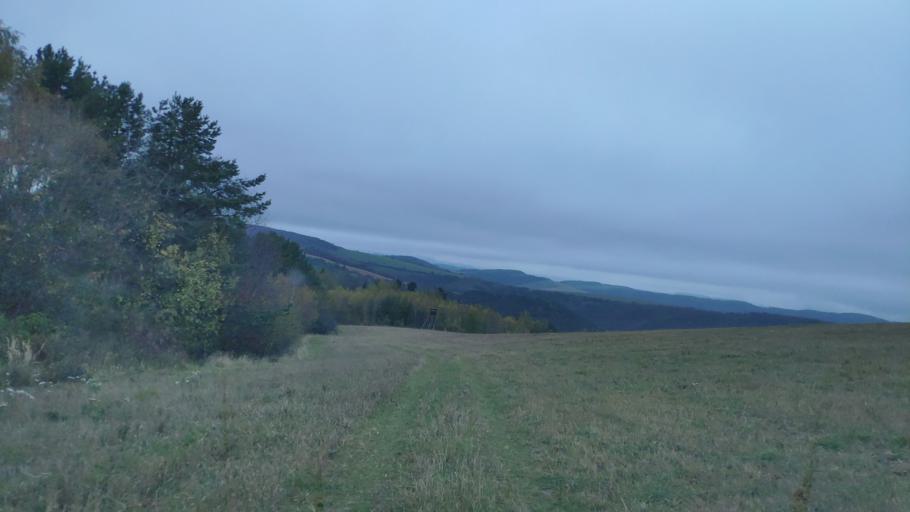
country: SK
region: Presovsky
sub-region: Okres Presov
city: Presov
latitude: 48.9329
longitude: 21.0864
